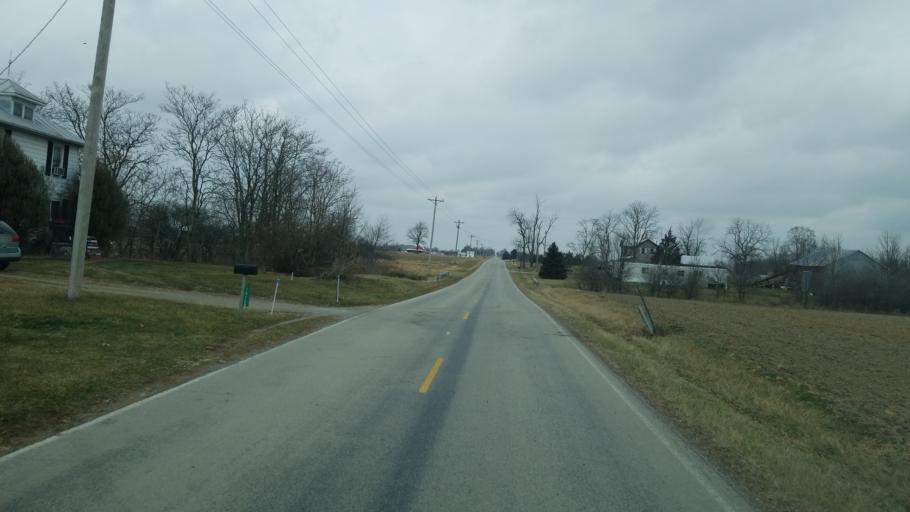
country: US
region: Ohio
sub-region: Hardin County
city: Forest
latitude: 40.7779
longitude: -83.4195
